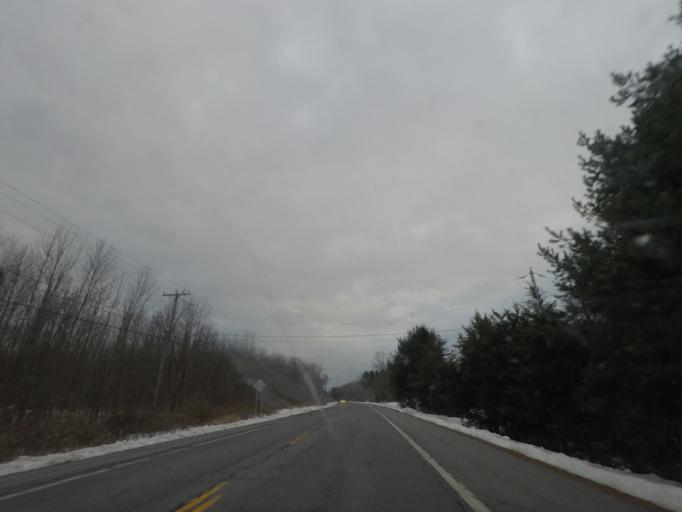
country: US
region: New York
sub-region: Ulster County
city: Plattekill
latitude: 41.6506
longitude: -74.1124
